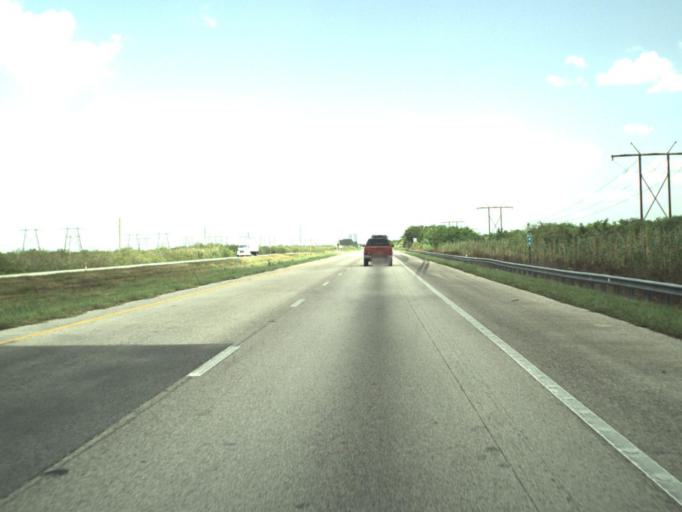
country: US
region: Florida
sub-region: Broward County
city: Weston
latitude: 26.3176
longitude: -80.5244
